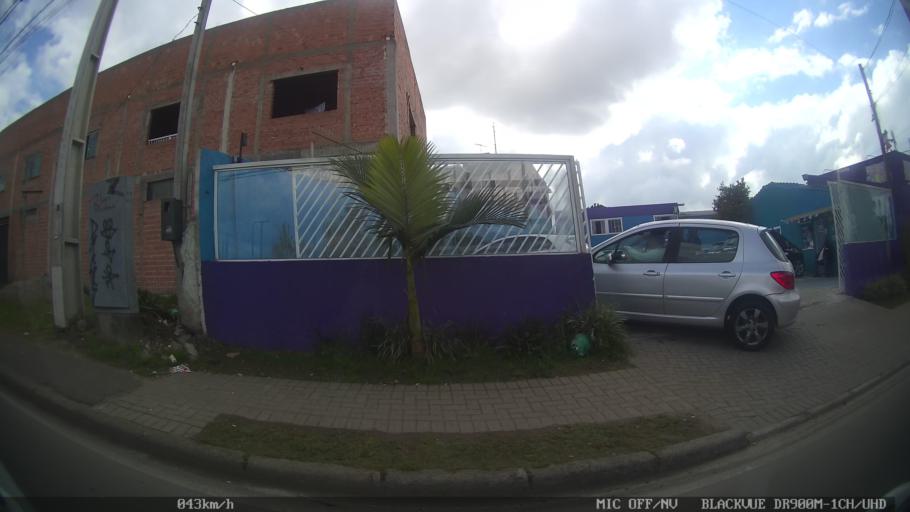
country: BR
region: Parana
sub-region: Colombo
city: Colombo
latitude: -25.3455
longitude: -49.1919
